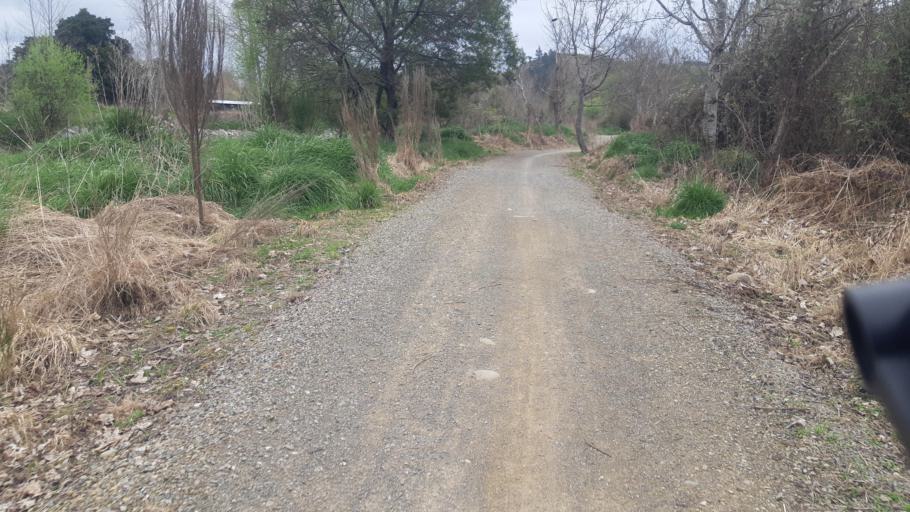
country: NZ
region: Tasman
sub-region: Tasman District
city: Wakefield
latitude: -41.4051
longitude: 173.0213
